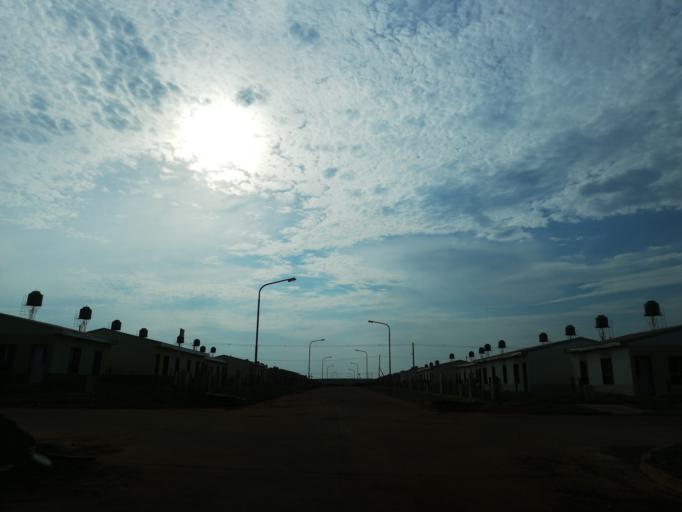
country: AR
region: Misiones
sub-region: Departamento de Capital
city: Posadas
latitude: -27.4035
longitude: -55.9901
